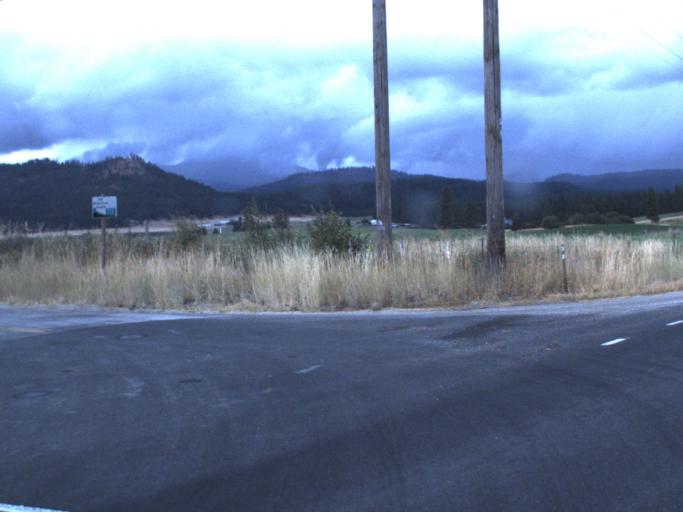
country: US
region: Washington
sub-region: Stevens County
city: Chewelah
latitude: 48.0923
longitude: -117.7578
